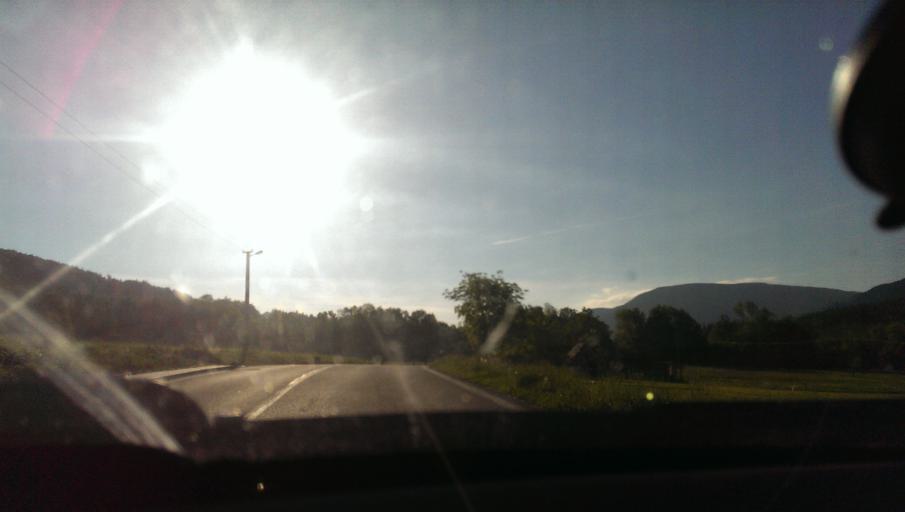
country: CZ
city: Kuncice pod Ondrejnikem
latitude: 49.5409
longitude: 18.2814
